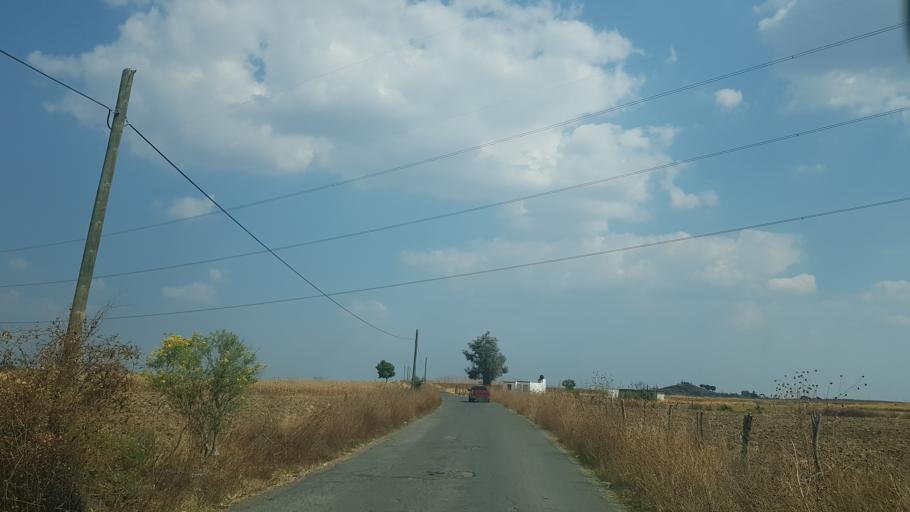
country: MX
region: Puebla
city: San Juan Amecac
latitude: 18.8235
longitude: -98.6556
